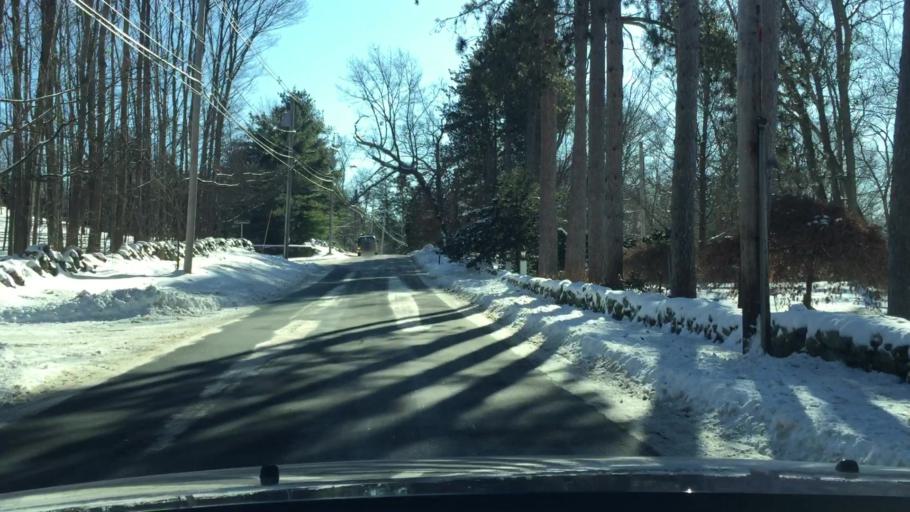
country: US
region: Massachusetts
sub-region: Essex County
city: North Andover
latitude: 42.6849
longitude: -71.0994
